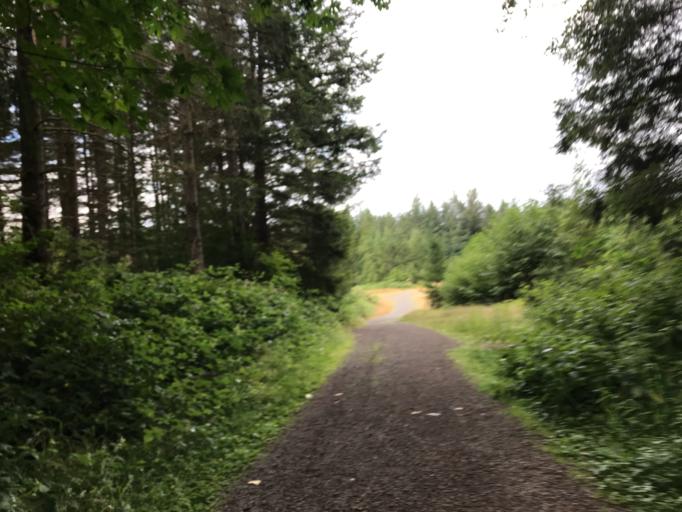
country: US
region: Washington
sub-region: King County
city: Ravensdale
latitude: 47.3503
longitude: -122.0081
